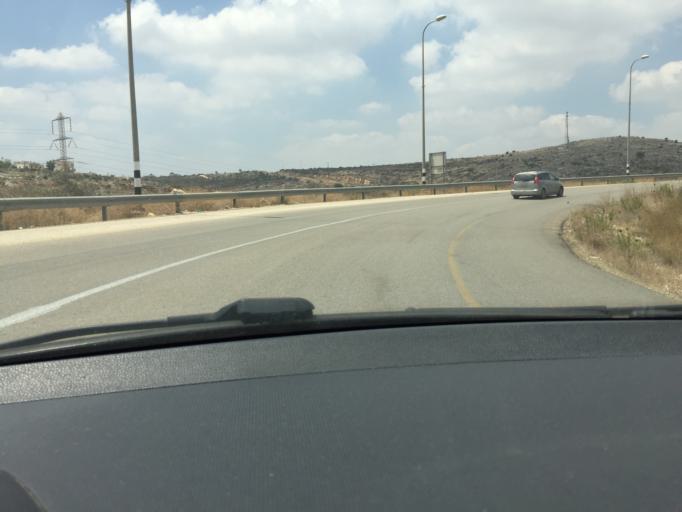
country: PS
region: West Bank
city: Sartah
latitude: 32.0929
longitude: 35.1069
